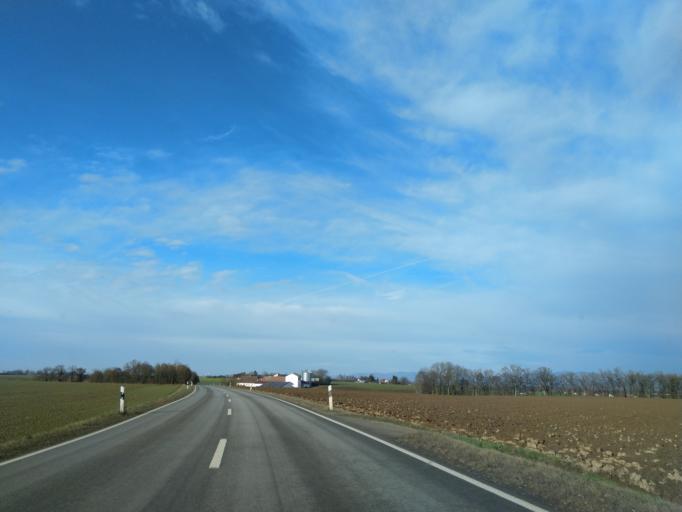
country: DE
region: Bavaria
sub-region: Lower Bavaria
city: Kunzing
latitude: 48.6602
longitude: 13.0450
